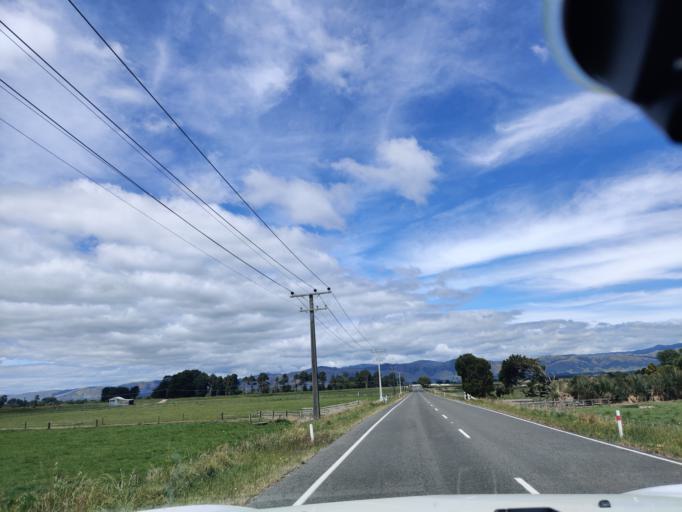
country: NZ
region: Manawatu-Wanganui
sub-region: Horowhenua District
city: Foxton
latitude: -40.4924
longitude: 175.3747
